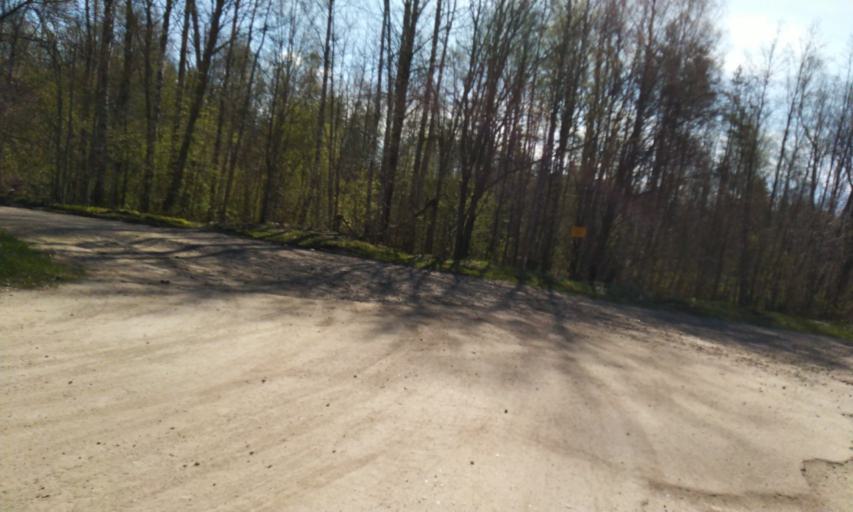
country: RU
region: Leningrad
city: Garbolovo
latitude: 60.3871
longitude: 30.4838
